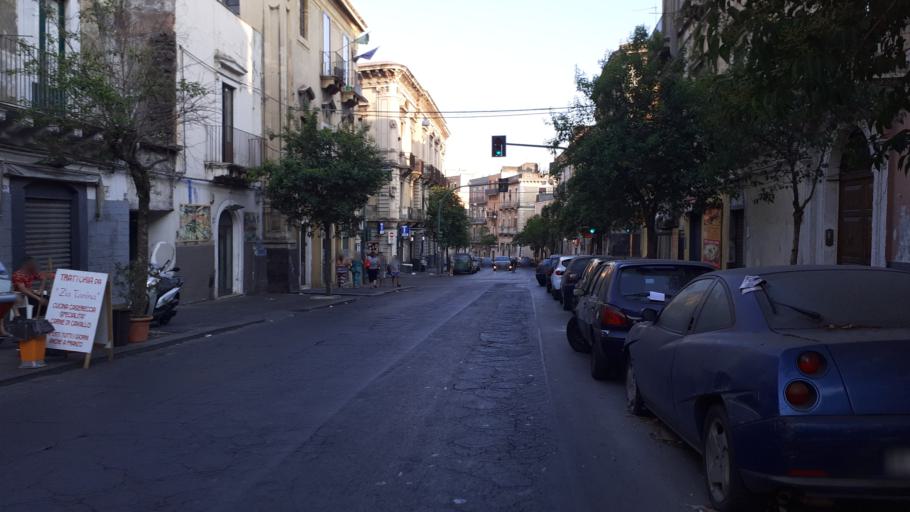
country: IT
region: Sicily
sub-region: Catania
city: Catania
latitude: 37.5005
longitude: 15.0760
